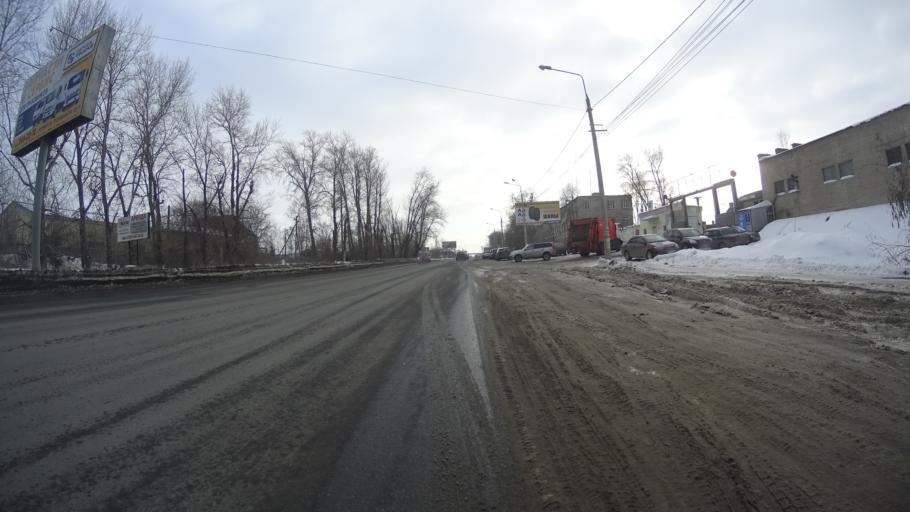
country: RU
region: Chelyabinsk
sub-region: Gorod Chelyabinsk
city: Chelyabinsk
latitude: 55.1243
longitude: 61.3858
